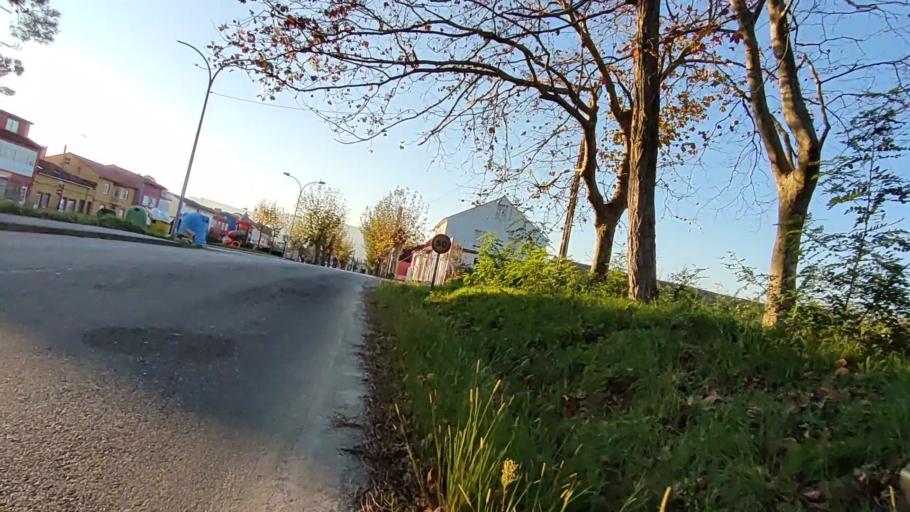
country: ES
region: Galicia
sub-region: Provincia da Coruna
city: Rianxo
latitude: 42.6395
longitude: -8.8588
